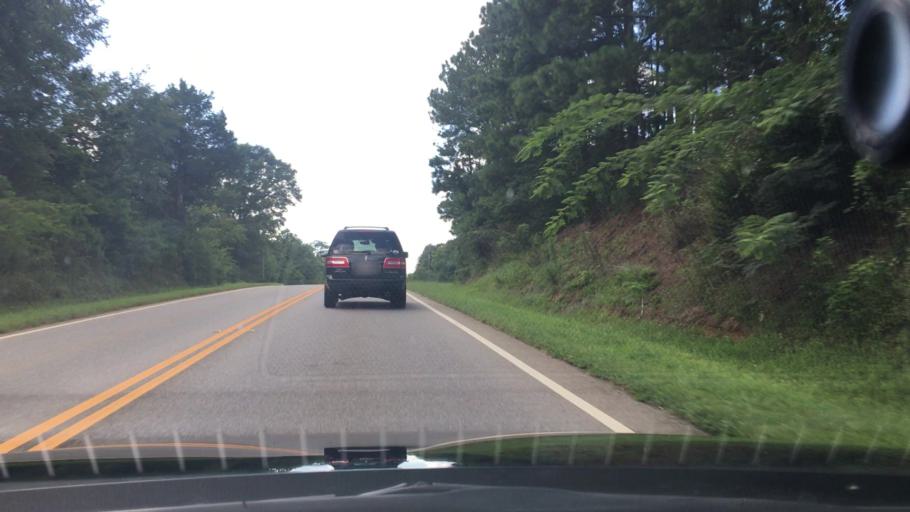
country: US
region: Georgia
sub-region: Putnam County
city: Eatonton
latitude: 33.3122
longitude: -83.4473
